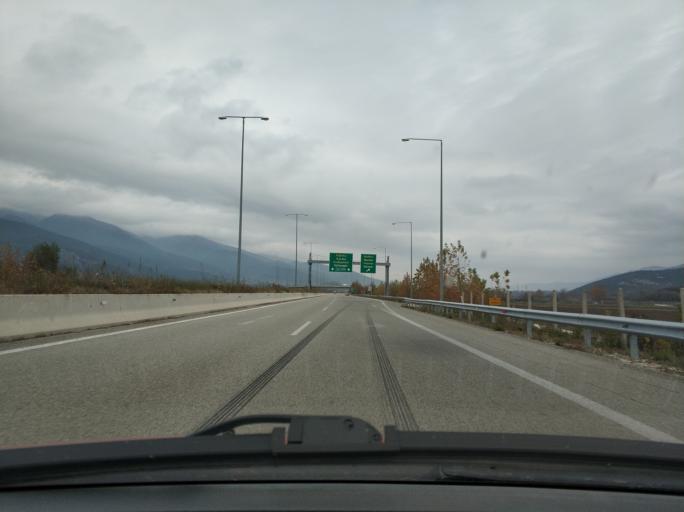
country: GR
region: East Macedonia and Thrace
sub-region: Nomos Kavalas
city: Nikisiani
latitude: 40.8367
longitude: 24.1120
